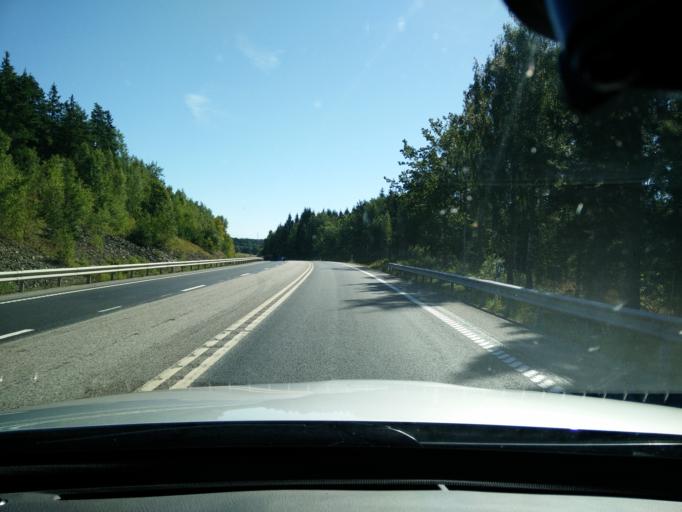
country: SE
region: Stockholm
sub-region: Lidingo
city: Lidingoe
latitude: 59.4530
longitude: 18.1815
